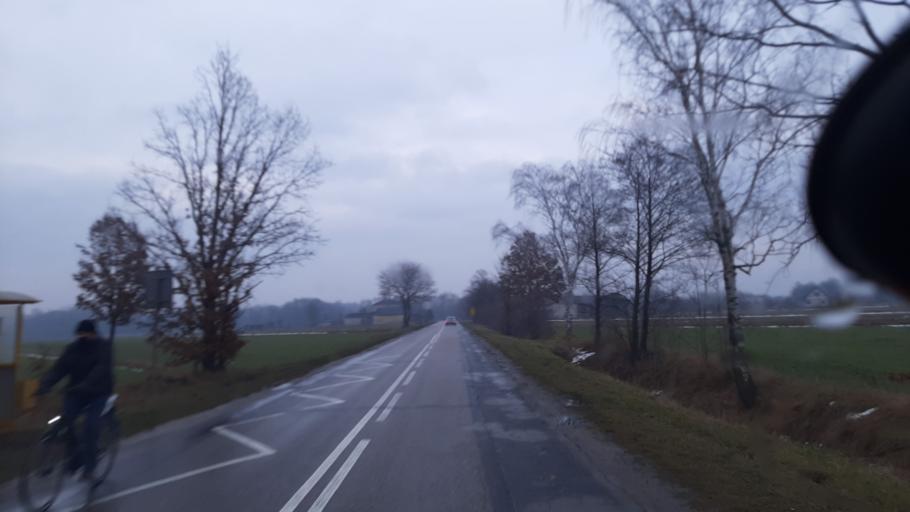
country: PL
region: Lublin Voivodeship
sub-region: Powiat lubartowski
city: Serniki
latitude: 51.4330
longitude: 22.6458
